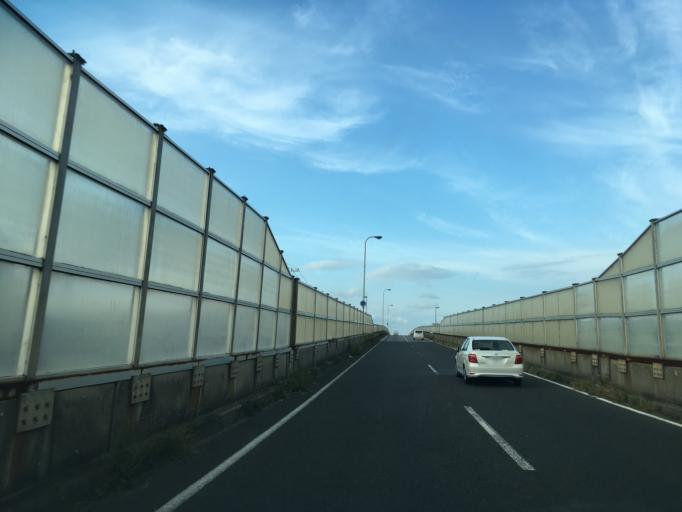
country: JP
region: Chiba
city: Kisarazu
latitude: 35.3664
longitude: 139.9250
